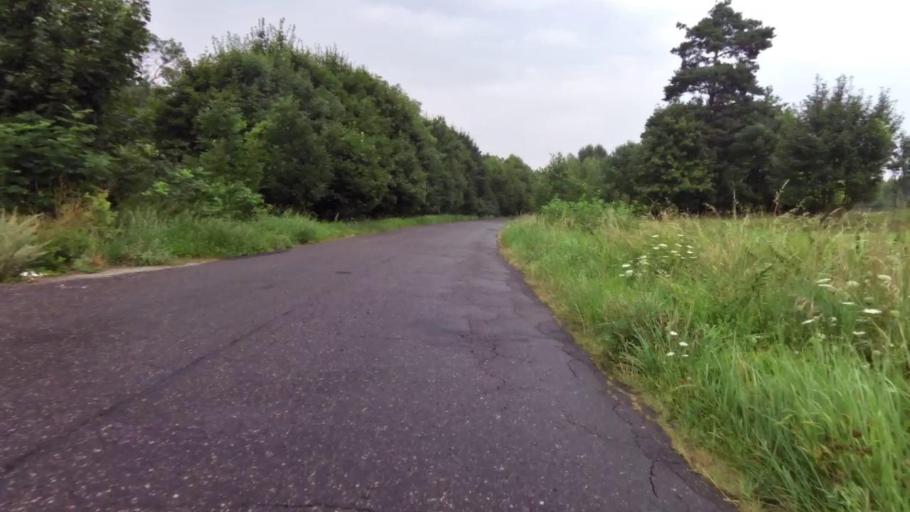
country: PL
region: West Pomeranian Voivodeship
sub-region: Powiat stargardzki
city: Insko
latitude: 53.4725
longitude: 15.5988
